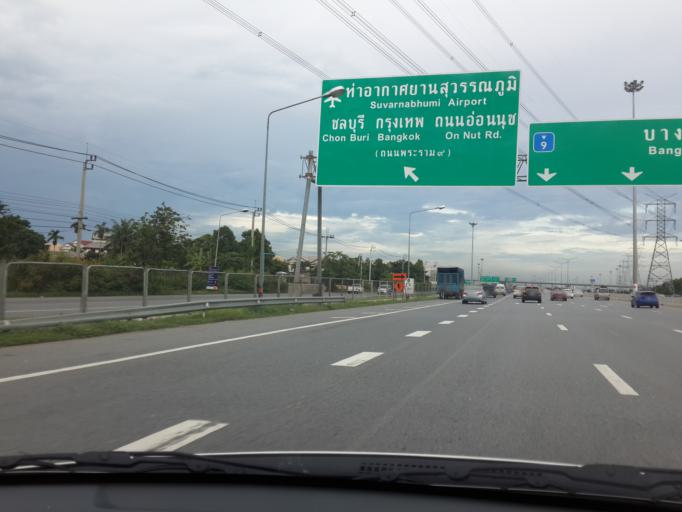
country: TH
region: Bangkok
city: Saphan Sung
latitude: 13.7442
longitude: 100.7028
